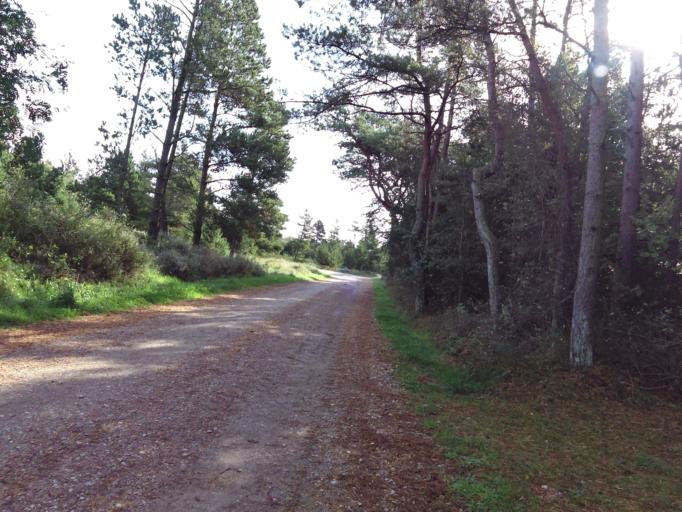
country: DK
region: South Denmark
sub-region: Varde Kommune
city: Oksbol
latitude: 55.5586
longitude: 8.2167
